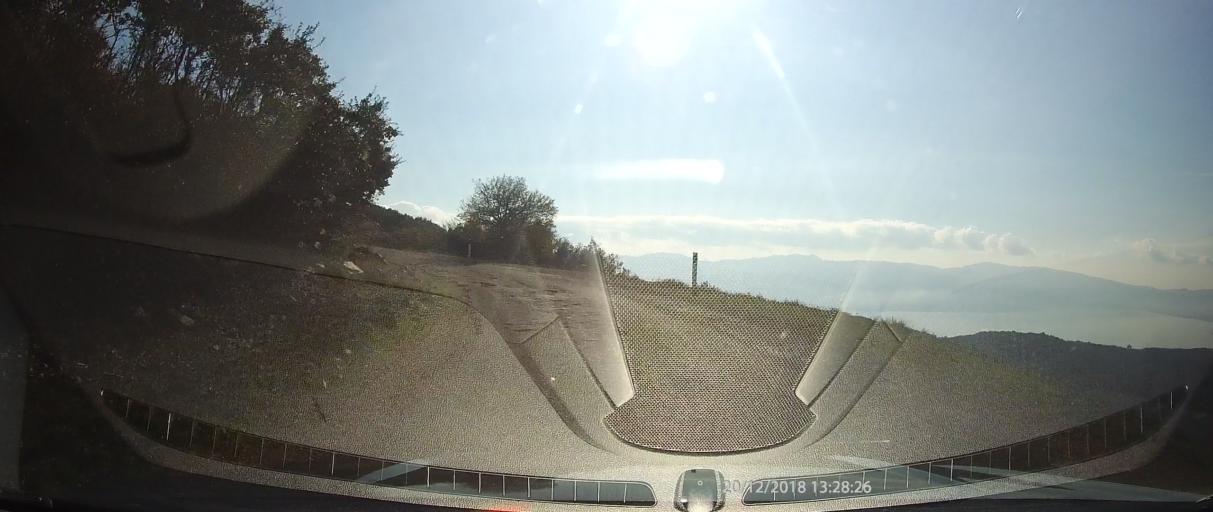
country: GR
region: West Greece
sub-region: Nomos Aitolias kai Akarnanias
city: Paravola
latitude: 38.6284
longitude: 21.5743
